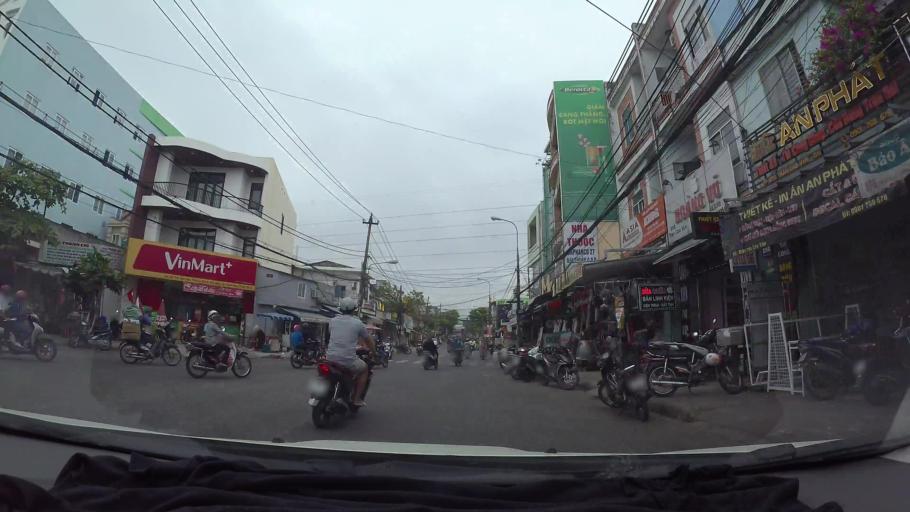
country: VN
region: Da Nang
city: Thanh Khe
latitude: 16.0676
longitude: 108.1821
